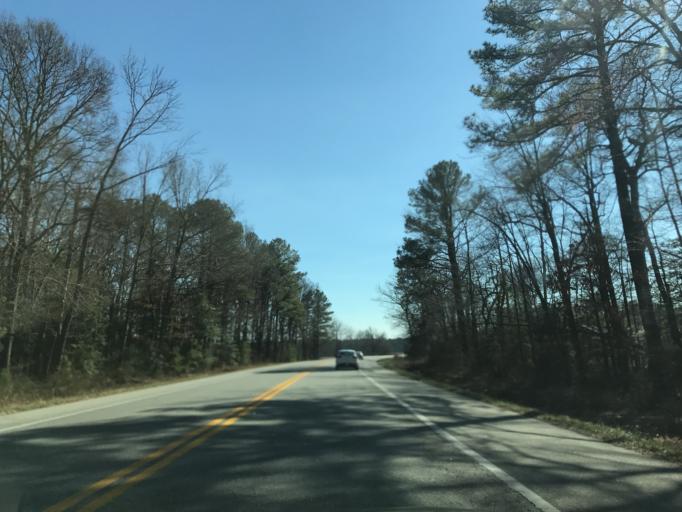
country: US
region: Maryland
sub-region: Queen Anne's County
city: Stevensville
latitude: 38.9353
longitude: -76.3548
